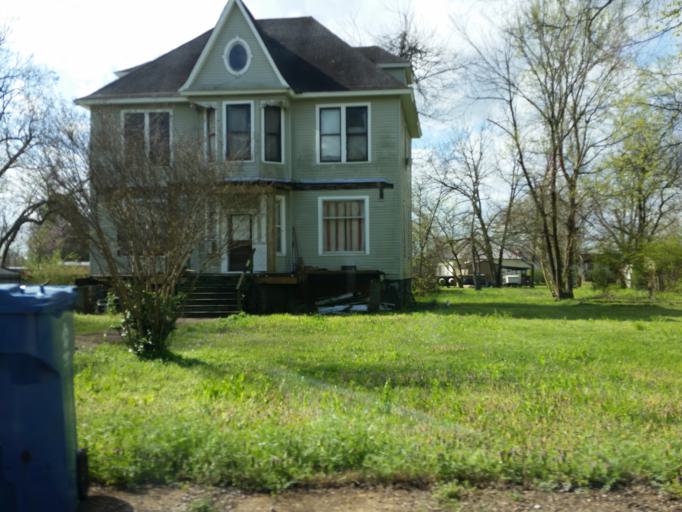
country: US
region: Missouri
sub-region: Butler County
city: Poplar Bluff
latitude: 36.7635
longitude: -90.3806
